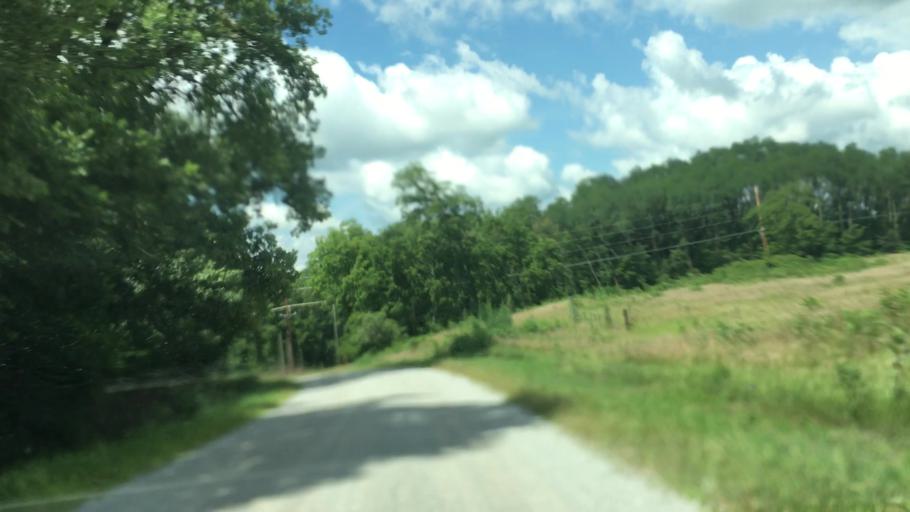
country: US
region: Iowa
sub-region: Linn County
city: Lisbon
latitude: 41.8288
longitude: -91.3840
